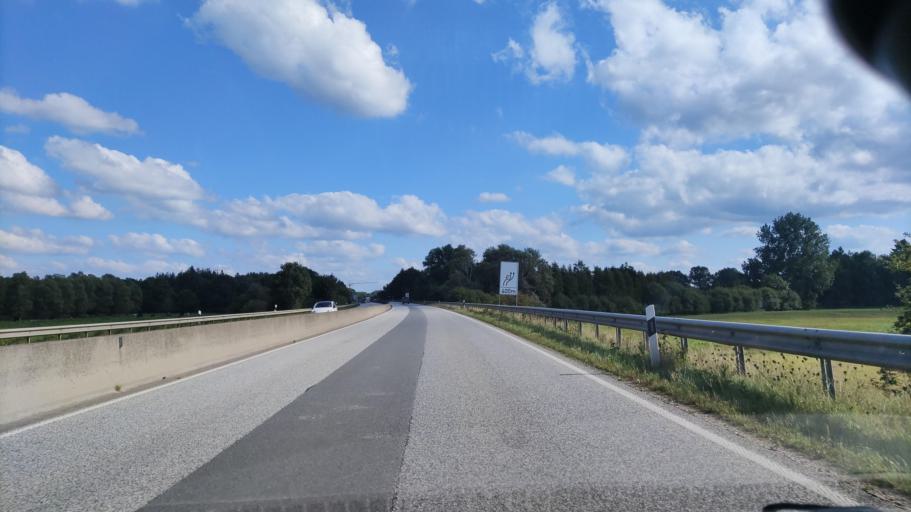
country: DE
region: Schleswig-Holstein
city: Westerronfeld
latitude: 54.3040
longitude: 9.6366
